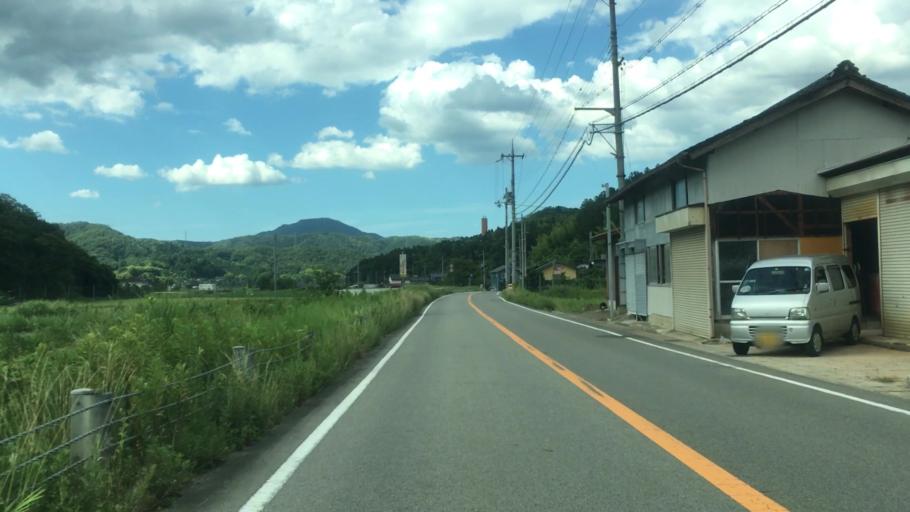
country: JP
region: Hyogo
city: Toyooka
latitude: 35.5383
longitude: 134.7899
